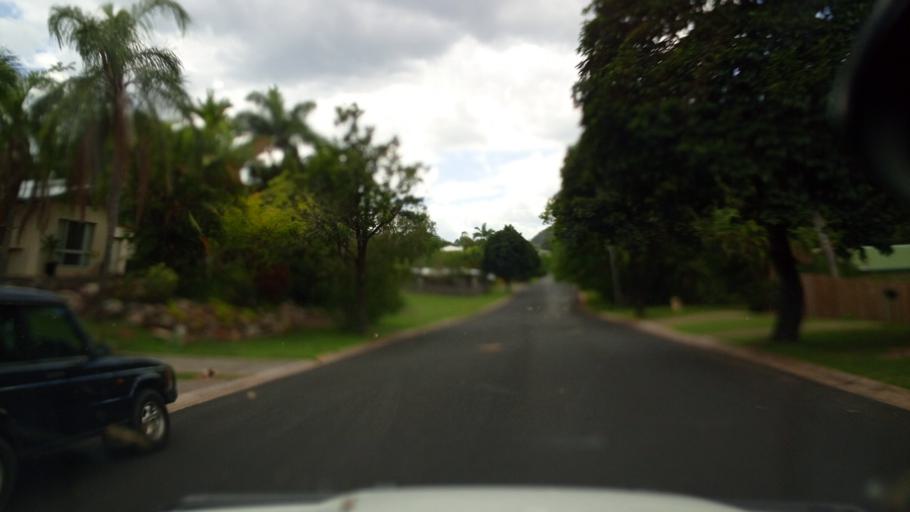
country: AU
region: Queensland
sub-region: Cairns
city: Redlynch
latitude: -16.9076
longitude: 145.7170
